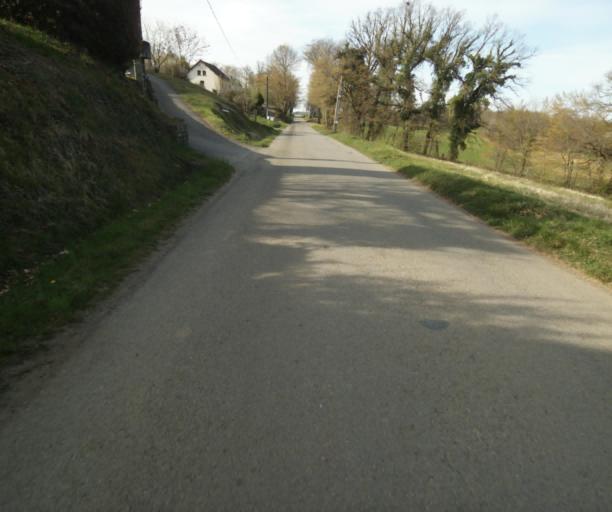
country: FR
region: Limousin
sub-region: Departement de la Correze
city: Naves
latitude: 45.2980
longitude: 1.7401
